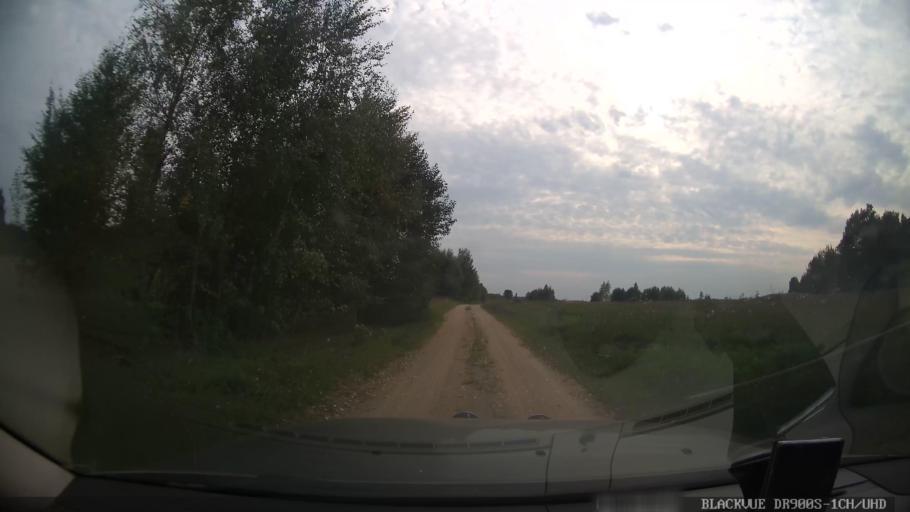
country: BY
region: Grodnenskaya
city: Ashmyany
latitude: 54.5353
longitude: 25.6736
